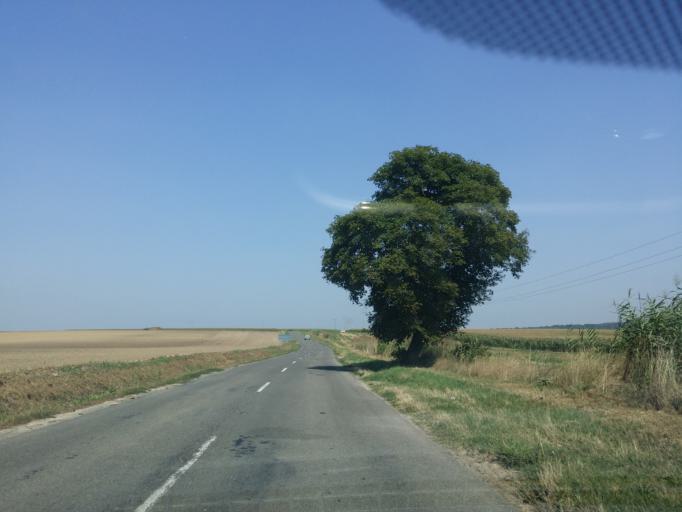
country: HU
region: Tolna
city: Hogyesz
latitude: 46.5393
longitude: 18.3564
